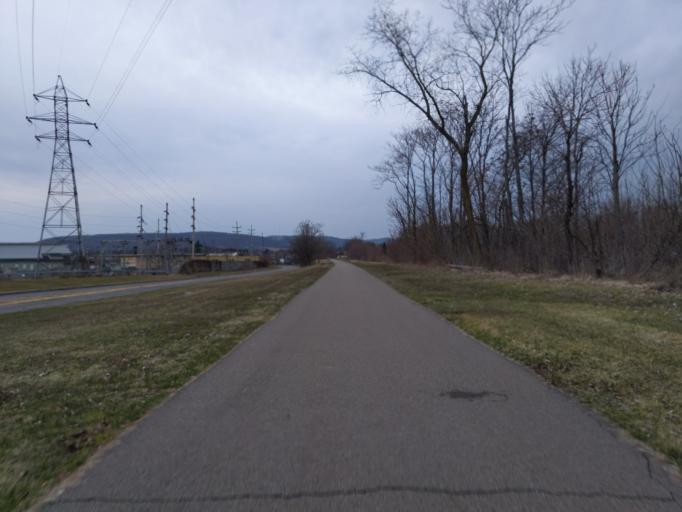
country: US
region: New York
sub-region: Chemung County
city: Elmira
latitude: 42.0983
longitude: -76.7980
